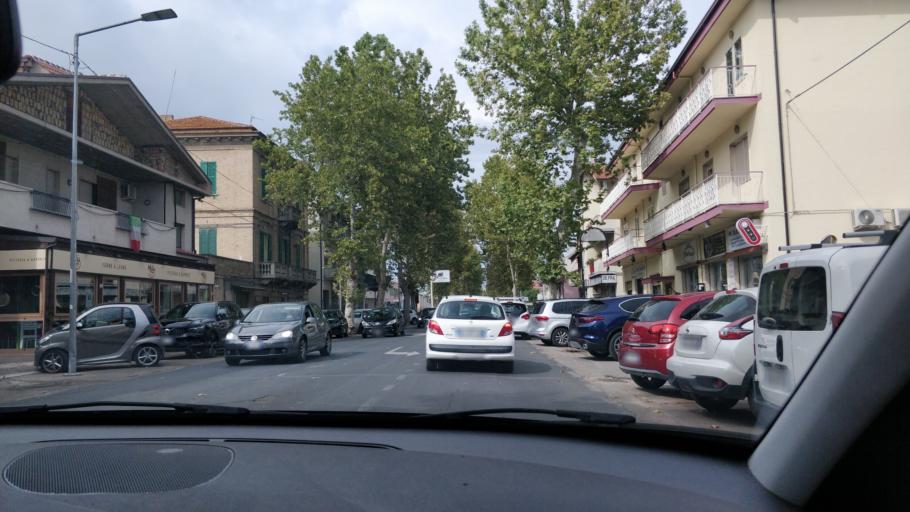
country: IT
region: Abruzzo
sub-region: Provincia di Chieti
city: Sambuceto
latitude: 42.4251
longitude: 14.1854
